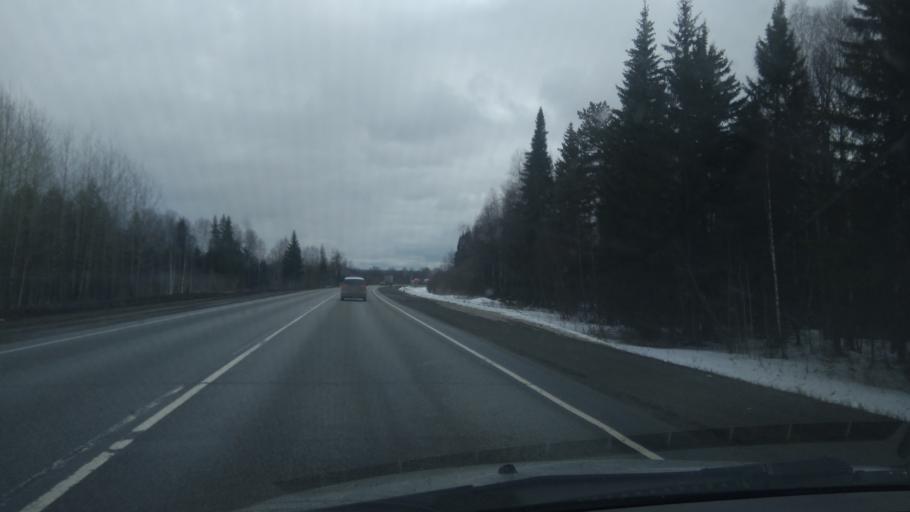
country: RU
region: Sverdlovsk
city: Ufimskiy
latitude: 56.7709
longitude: 58.1184
